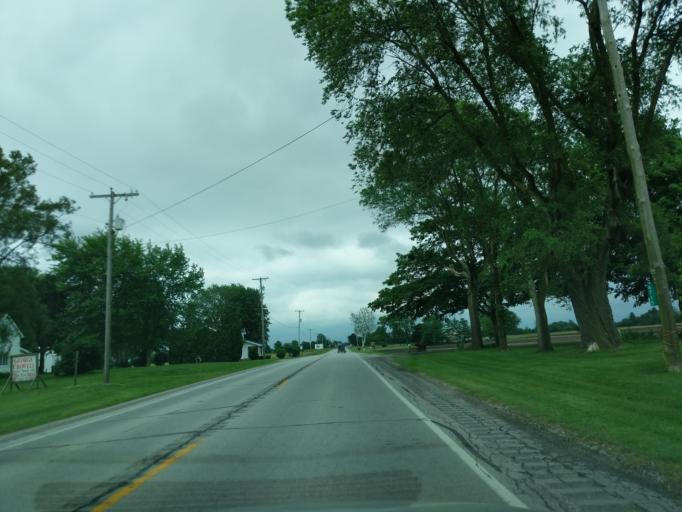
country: US
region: Indiana
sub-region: Madison County
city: Elwood
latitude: 40.2774
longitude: -85.7995
